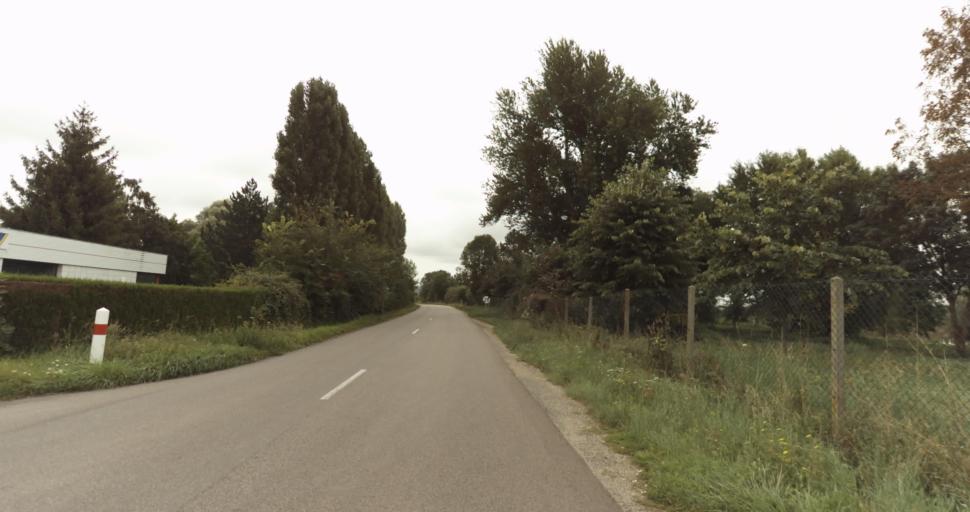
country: FR
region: Haute-Normandie
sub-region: Departement de l'Eure
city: Garennes-sur-Eure
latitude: 48.9186
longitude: 1.4525
